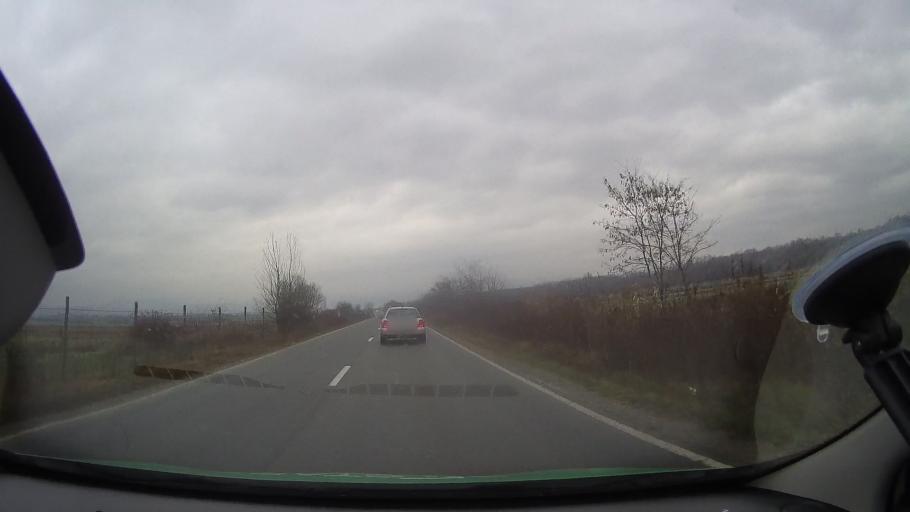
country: RO
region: Arad
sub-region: Comuna Almas
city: Almas
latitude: 46.2815
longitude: 22.2765
